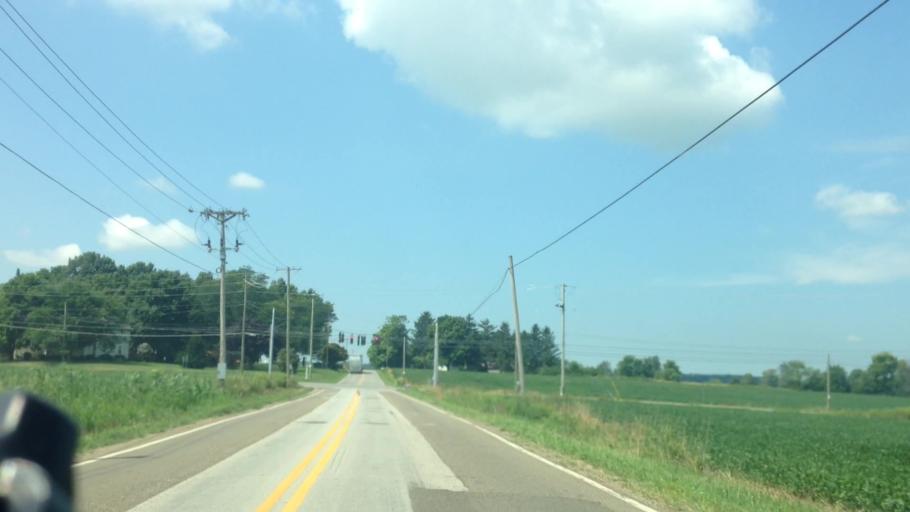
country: US
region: Ohio
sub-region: Wayne County
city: Orrville
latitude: 40.8694
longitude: -81.7620
